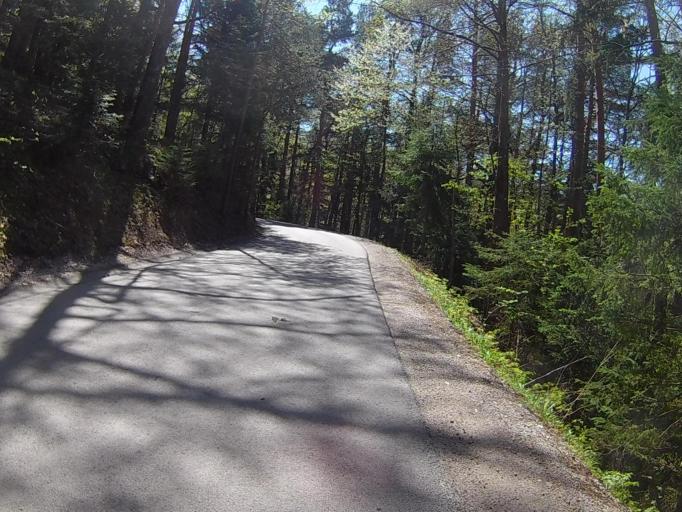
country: SI
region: Ruse
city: Ruse
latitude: 46.5291
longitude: 15.5097
